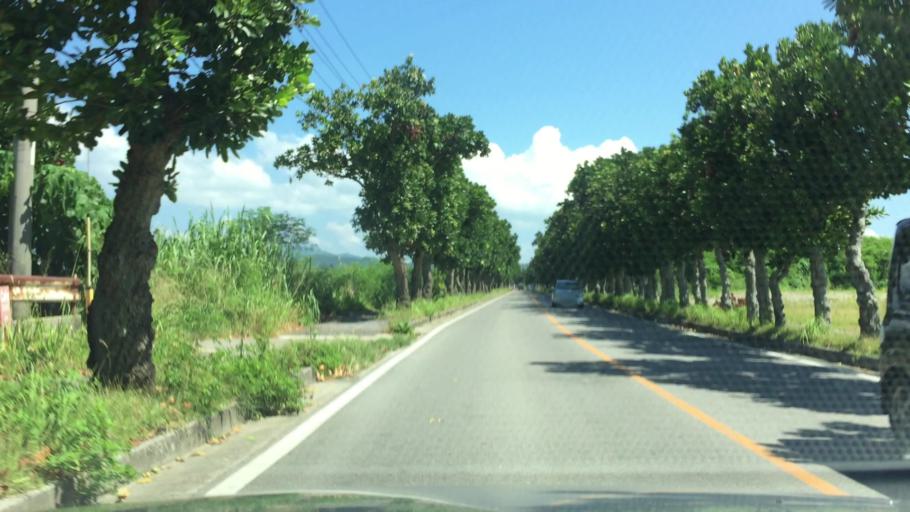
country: JP
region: Okinawa
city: Ishigaki
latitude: 24.3657
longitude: 124.2465
